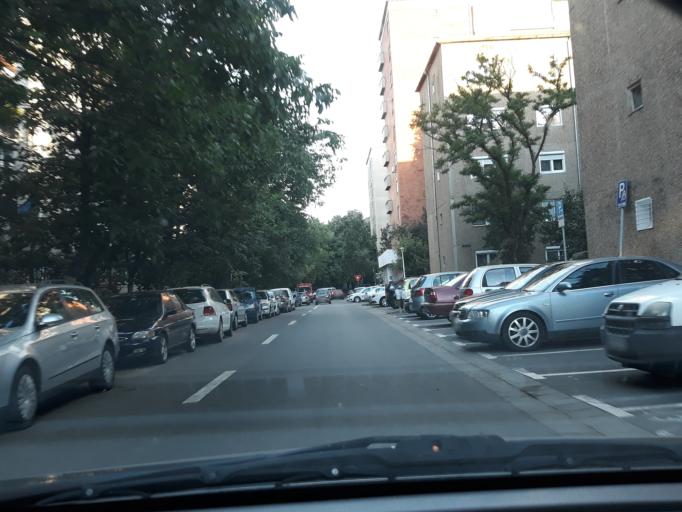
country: RO
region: Bihor
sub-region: Comuna Biharea
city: Oradea
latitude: 47.0802
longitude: 21.9185
